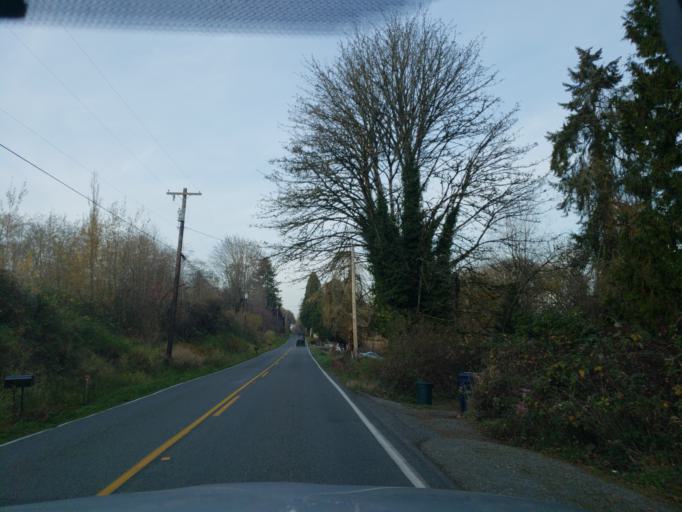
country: US
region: Washington
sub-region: Snohomish County
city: Cathcart
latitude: 47.8474
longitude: -122.0928
